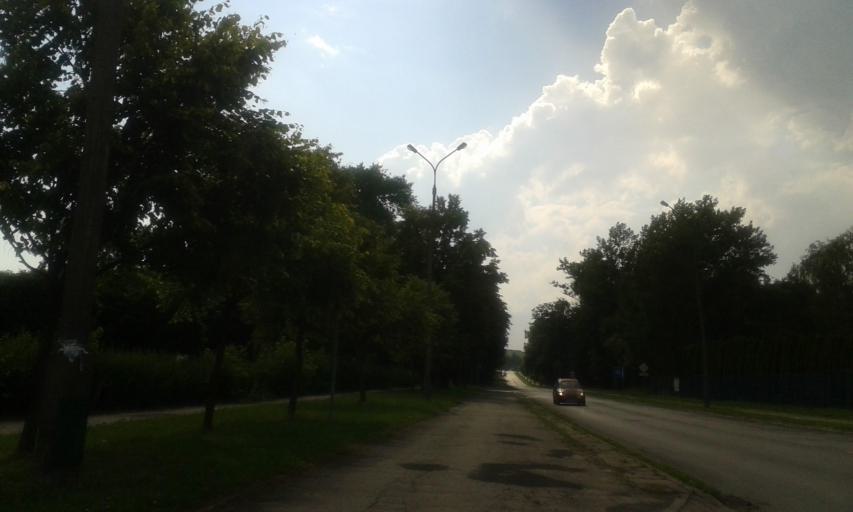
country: PL
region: Lesser Poland Voivodeship
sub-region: Powiat oswiecimski
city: Zaborze
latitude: 50.0354
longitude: 19.2526
